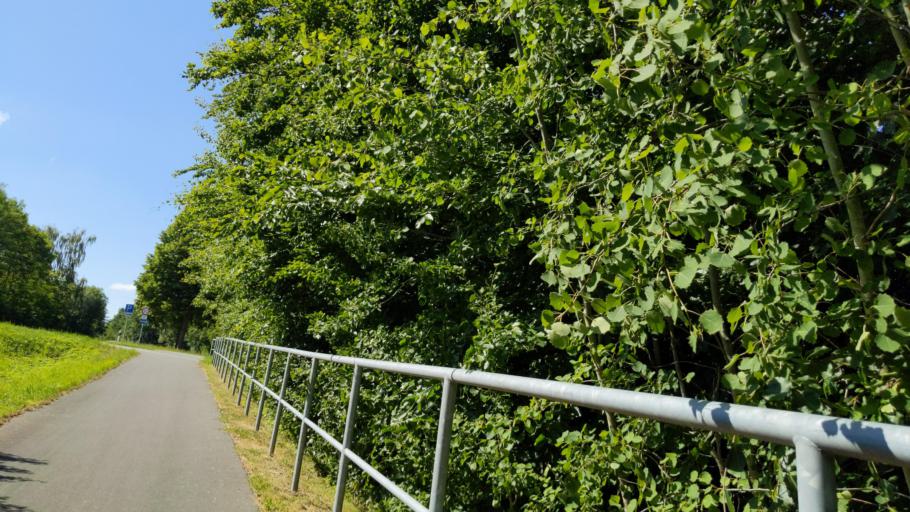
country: DE
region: Schleswig-Holstein
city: Kulpin
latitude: 53.7201
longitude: 10.6806
